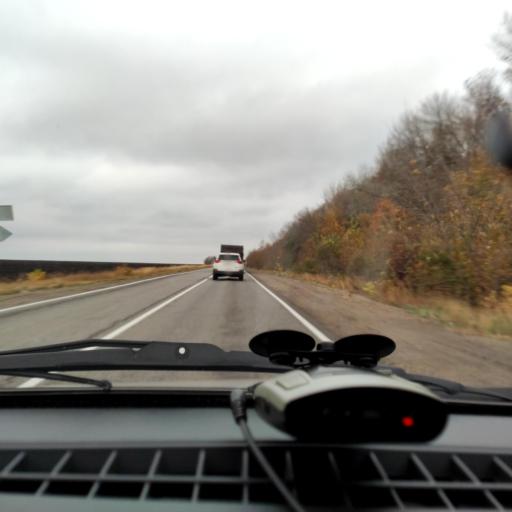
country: RU
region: Voronezj
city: Shilovo
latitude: 51.3852
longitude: 39.0080
